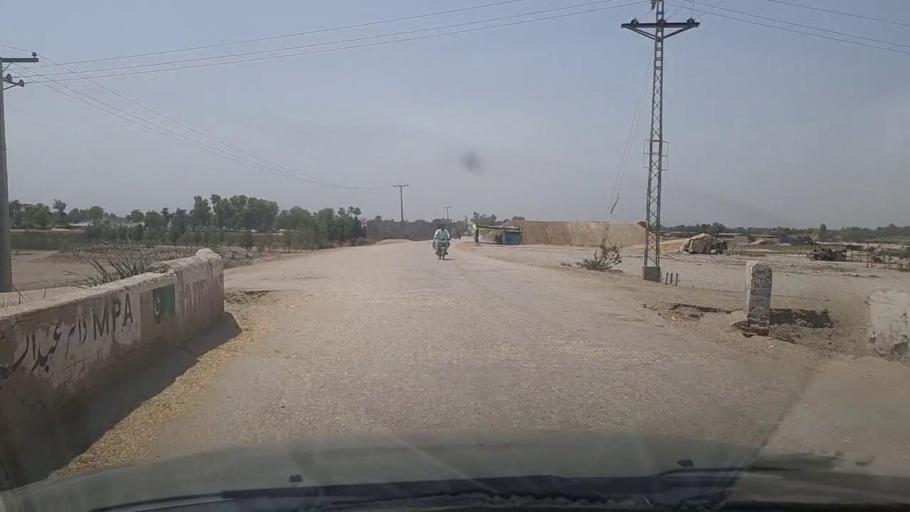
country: PK
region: Sindh
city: Bhiria
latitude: 26.8893
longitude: 68.2661
